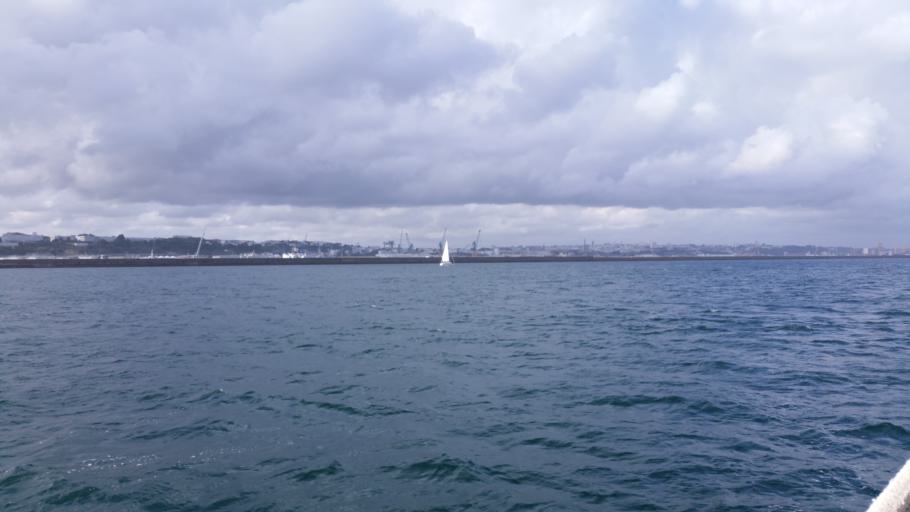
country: FR
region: Brittany
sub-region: Departement du Finistere
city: Roscanvel
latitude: 48.3566
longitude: -4.5156
